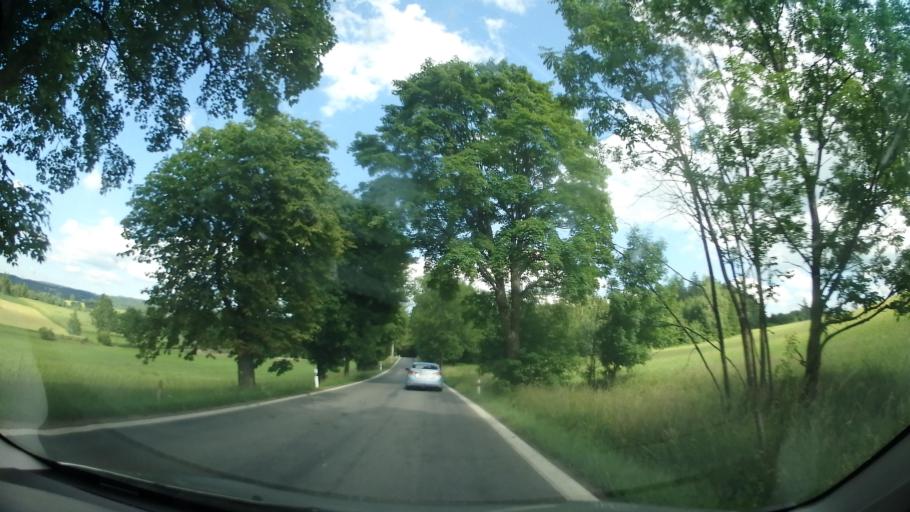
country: CZ
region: Vysocina
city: Zd'ar nad Sazavou Druhy
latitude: 49.6169
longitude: 15.9423
